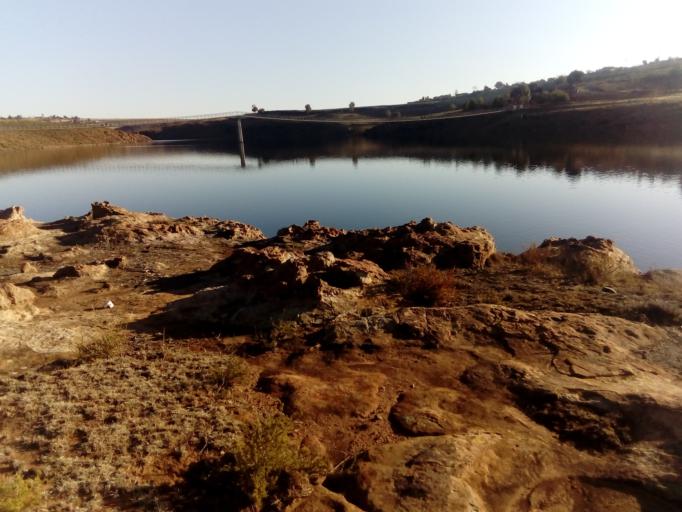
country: LS
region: Berea
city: Teyateyaneng
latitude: -29.3220
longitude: 27.8186
